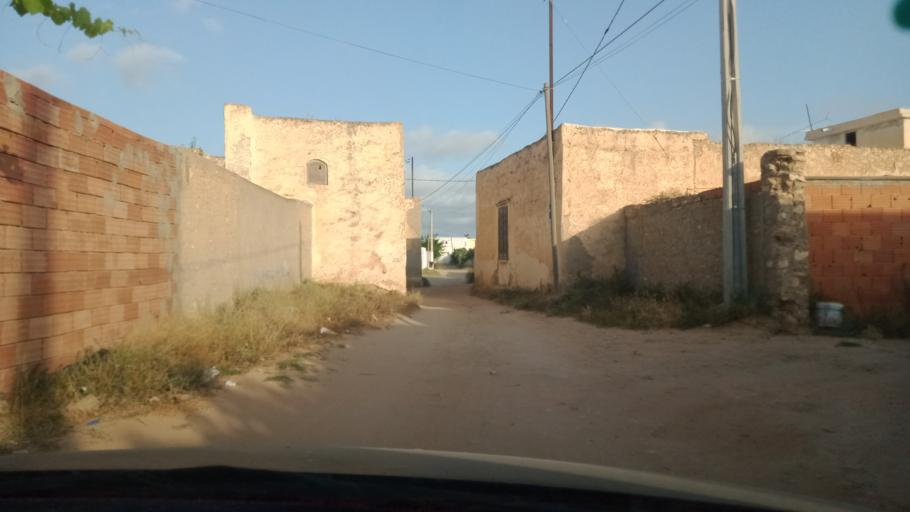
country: TN
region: Safaqis
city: Al Qarmadah
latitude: 34.8179
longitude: 10.7504
